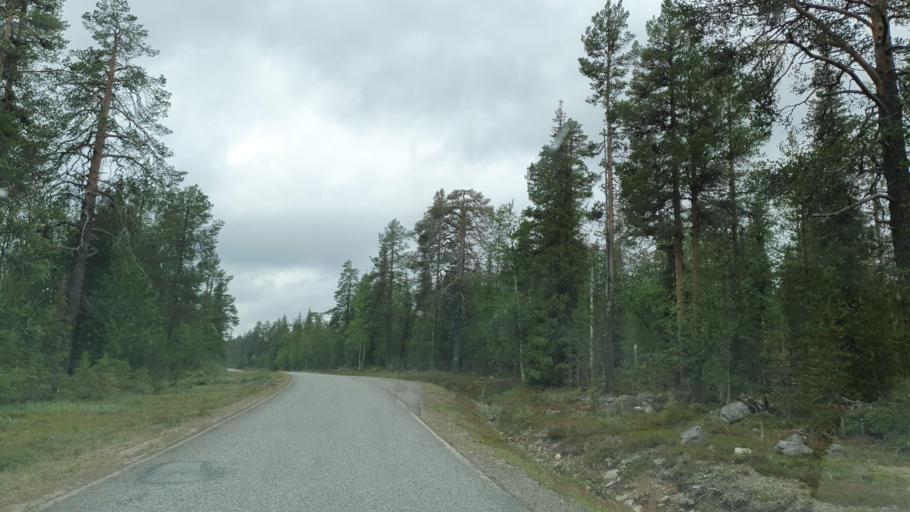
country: FI
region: Lapland
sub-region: Tunturi-Lappi
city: Muonio
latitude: 67.7295
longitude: 24.2536
